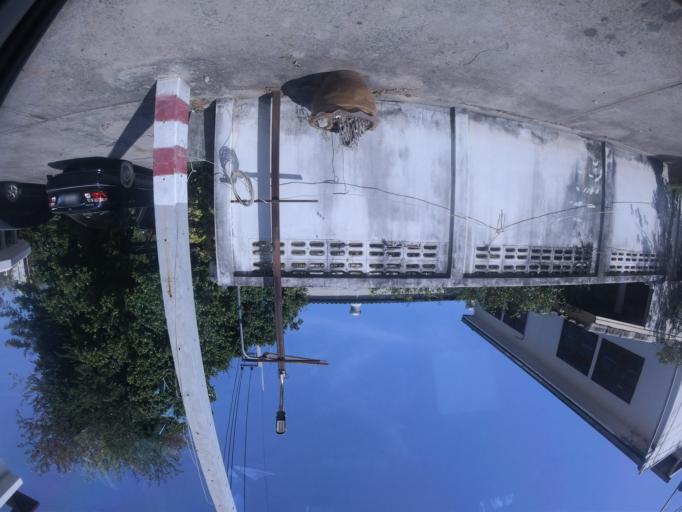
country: TH
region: Maha Sarakham
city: Chiang Yuen
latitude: 16.3770
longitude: 102.9681
